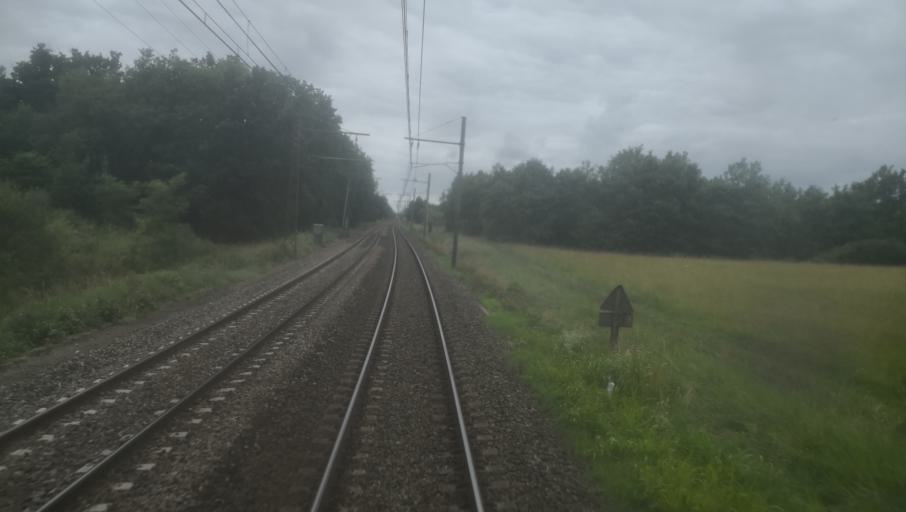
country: FR
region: Midi-Pyrenees
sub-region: Departement du Tarn-et-Garonne
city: Finhan
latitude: 43.8935
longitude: 1.2702
